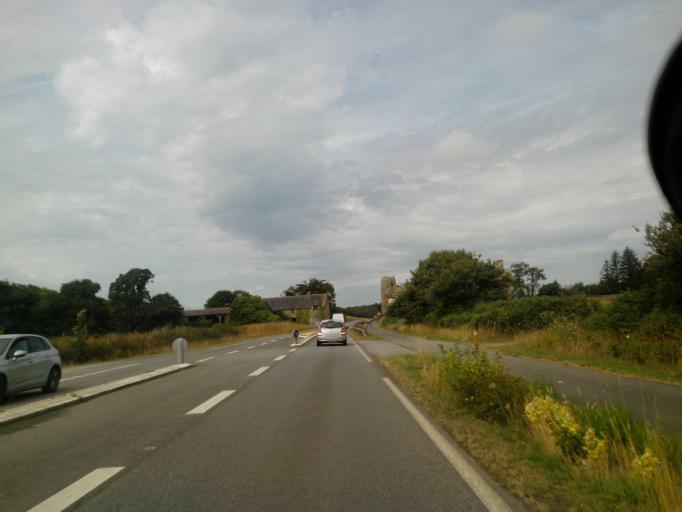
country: FR
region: Brittany
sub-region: Departement du Morbihan
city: Erdeven
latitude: 47.6418
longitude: -3.1351
